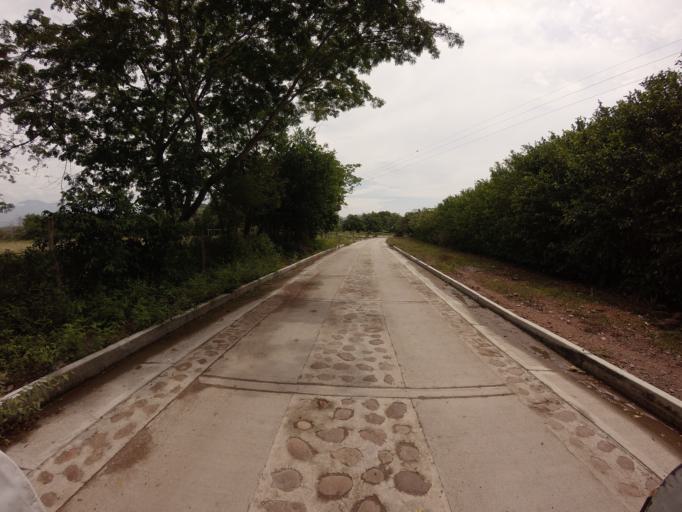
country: CO
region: Tolima
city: Natagaima
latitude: 3.4617
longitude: -75.1395
